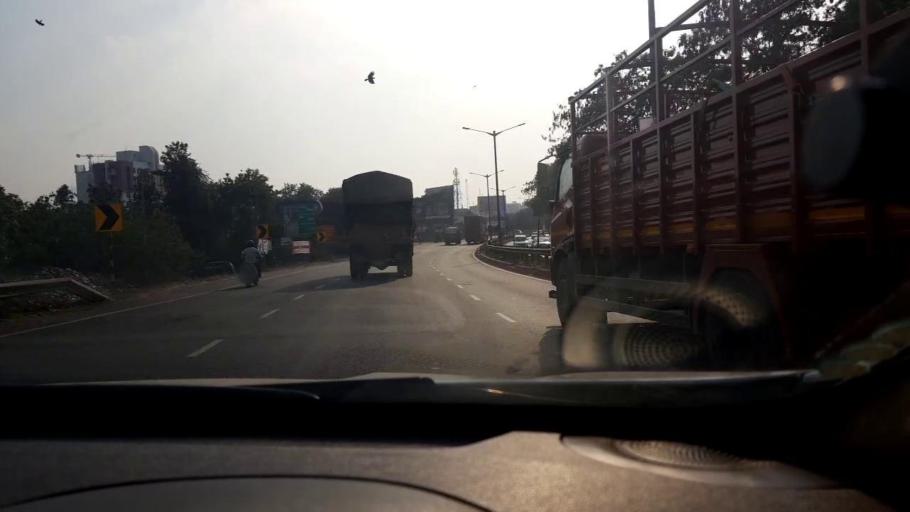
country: IN
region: Maharashtra
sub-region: Pune Division
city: Shivaji Nagar
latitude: 18.5292
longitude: 73.7786
